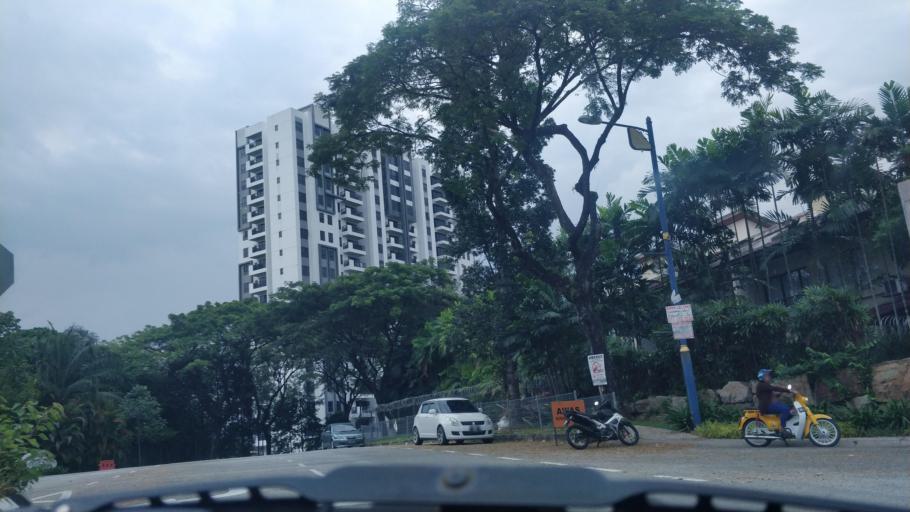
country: MY
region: Selangor
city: Kuang
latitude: 3.2086
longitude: 101.5809
